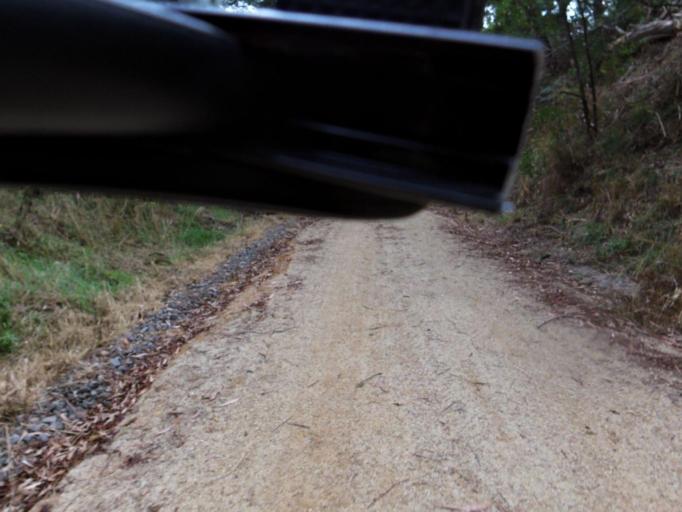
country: AU
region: Victoria
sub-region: Bass Coast
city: North Wonthaggi
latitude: -38.3899
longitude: 145.7169
